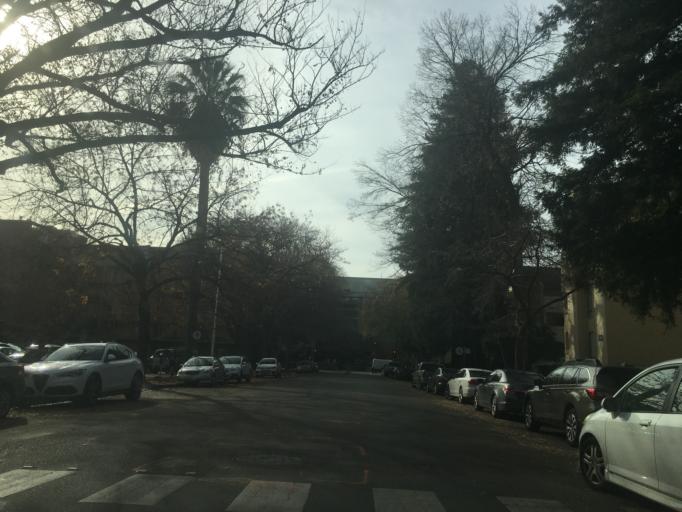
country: US
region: California
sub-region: Sacramento County
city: Sacramento
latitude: 38.5770
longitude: -121.5039
